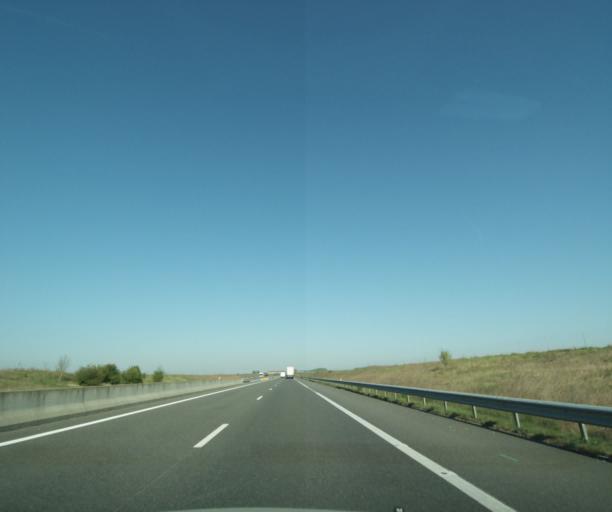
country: FR
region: Centre
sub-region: Departement du Loiret
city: Beaune-la-Rolande
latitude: 48.0887
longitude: 2.4301
